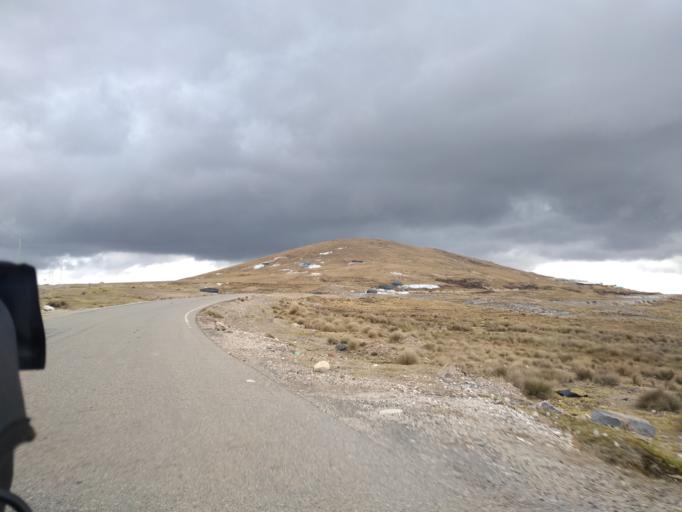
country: PE
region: La Libertad
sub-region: Provincia de Santiago de Chuco
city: Quiruvilca
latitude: -7.9934
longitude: -78.2937
